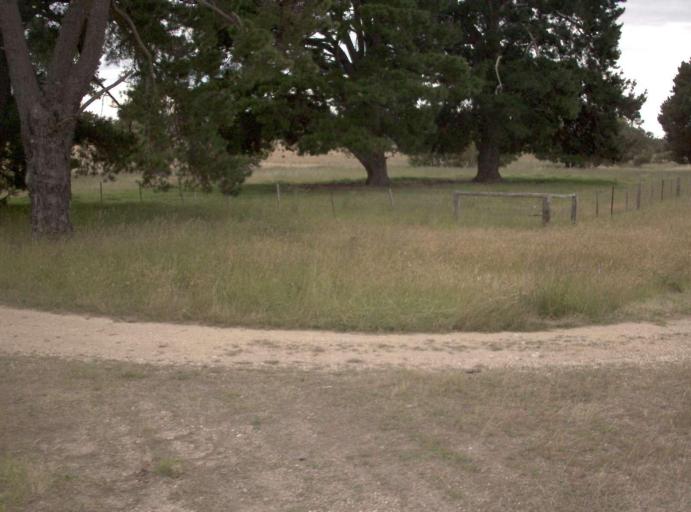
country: AU
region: Victoria
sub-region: East Gippsland
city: Bairnsdale
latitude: -37.9782
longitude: 147.4618
